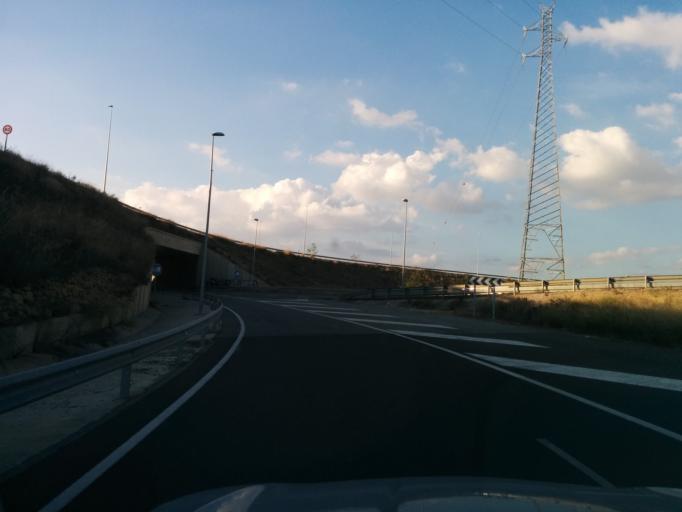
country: ES
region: Andalusia
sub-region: Provincia de Sevilla
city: Alcala de Guadaira
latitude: 37.3614
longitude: -5.8714
